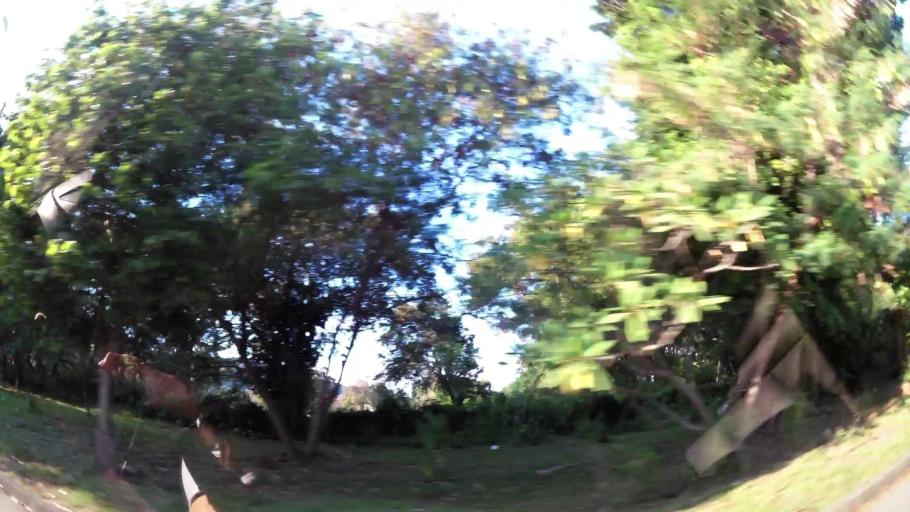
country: CO
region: Valle del Cauca
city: Cali
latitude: 3.4018
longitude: -76.5540
